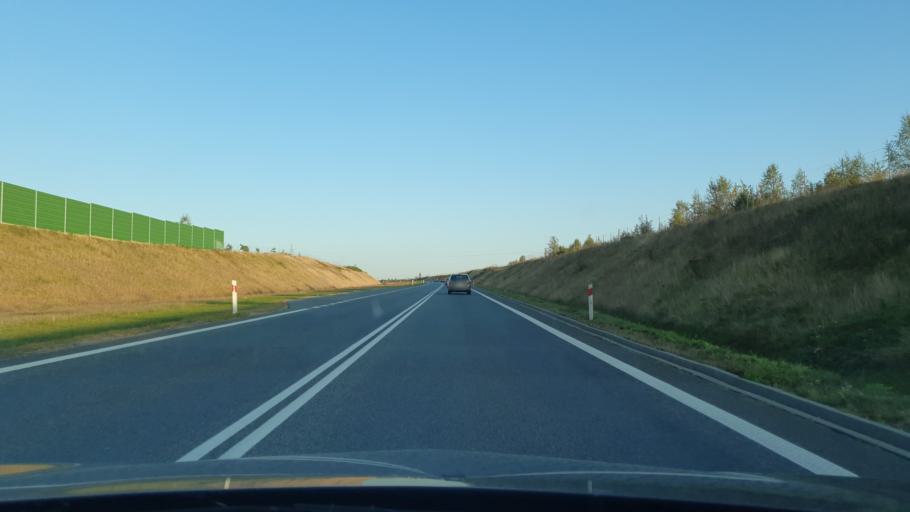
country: PL
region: Pomeranian Voivodeship
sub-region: Powiat slupski
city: Kobylnica
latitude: 54.4291
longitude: 16.9788
